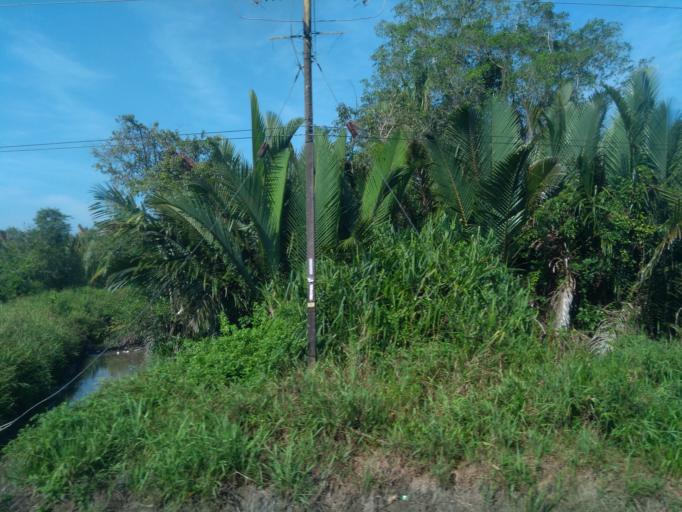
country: MY
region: Sarawak
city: Kuching
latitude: 1.6569
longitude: 110.4399
